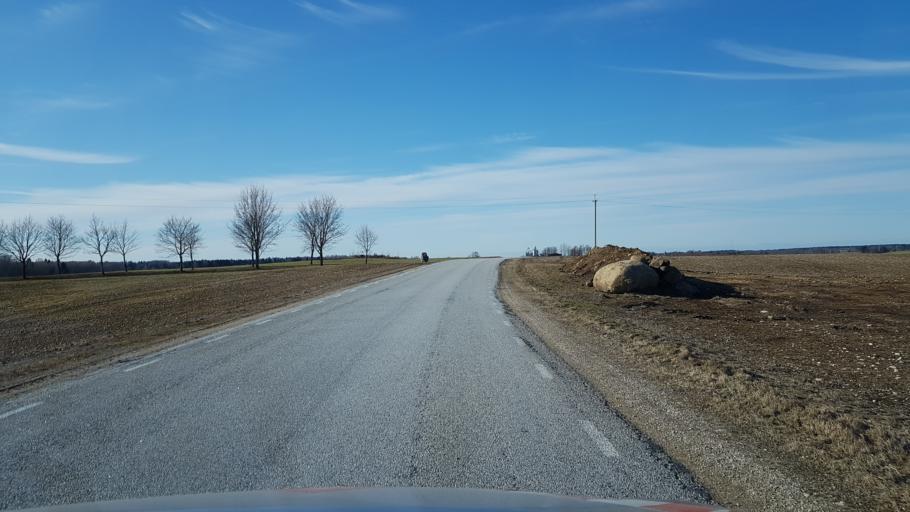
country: EE
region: Laeaene-Virumaa
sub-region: Kadrina vald
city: Kadrina
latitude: 59.2860
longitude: 26.1789
